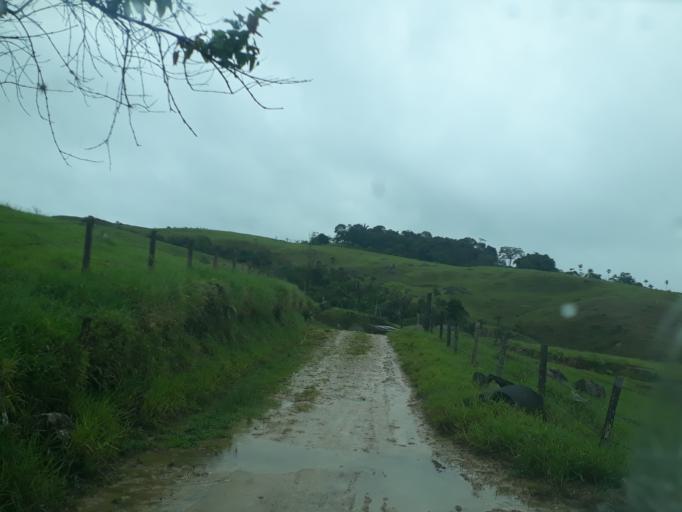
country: CO
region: Cundinamarca
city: Medina
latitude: 4.5364
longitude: -73.3866
